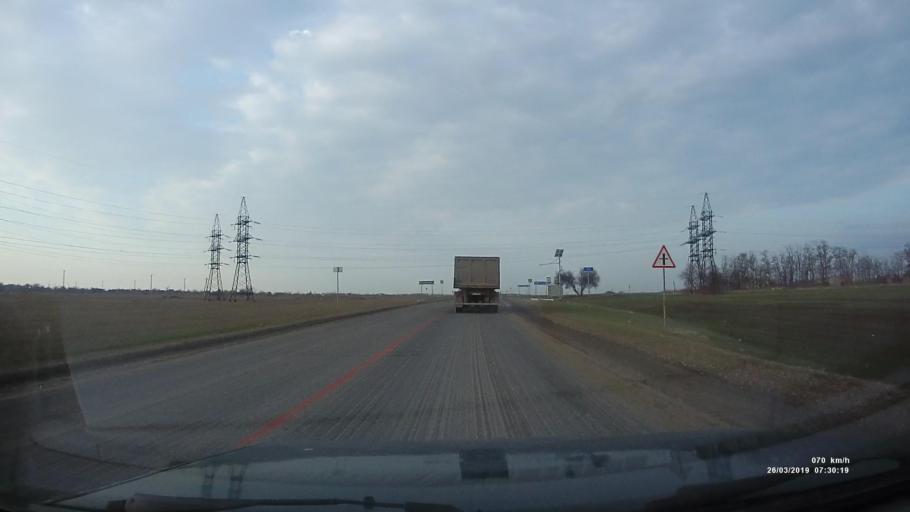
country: RU
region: Rostov
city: Novobessergenovka
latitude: 47.2374
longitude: 38.8078
